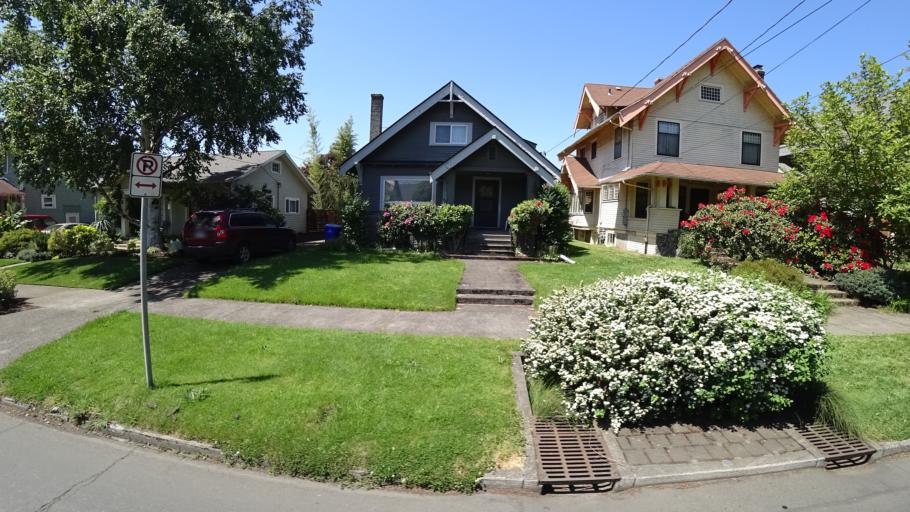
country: US
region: Oregon
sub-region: Multnomah County
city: Portland
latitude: 45.5360
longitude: -122.6240
